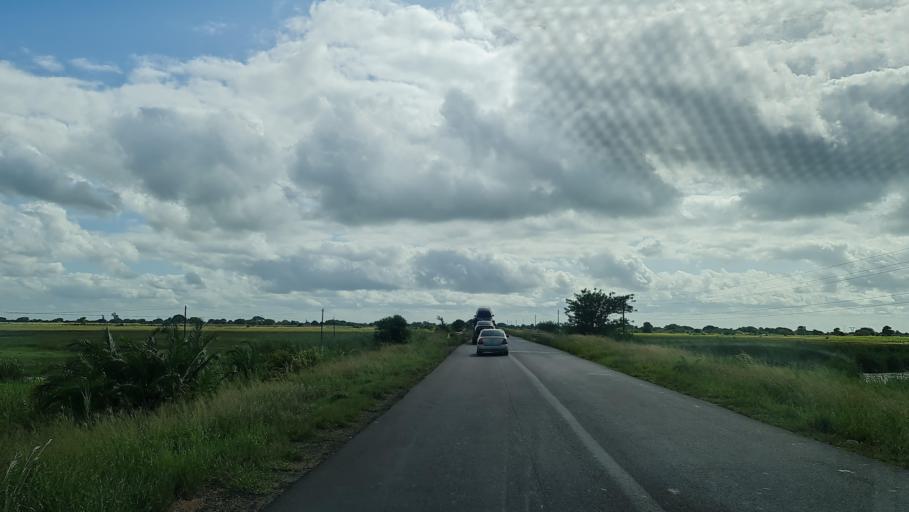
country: MZ
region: Gaza
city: Macia
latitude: -25.0949
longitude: 32.8328
